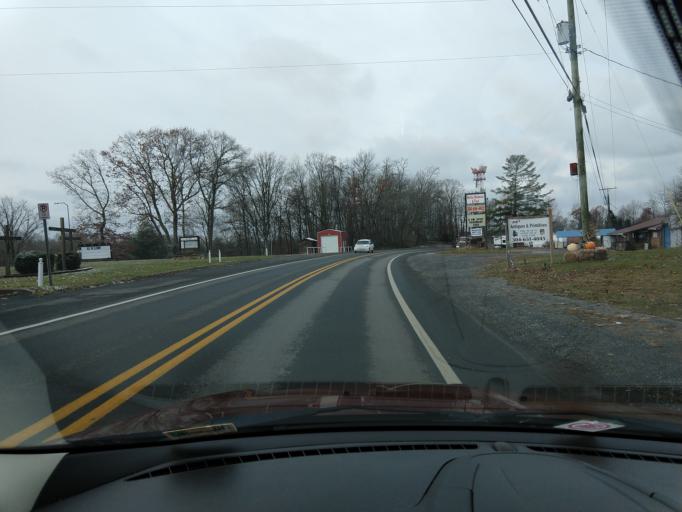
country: US
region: West Virginia
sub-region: Nicholas County
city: Craigsville
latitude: 38.2278
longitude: -80.6931
